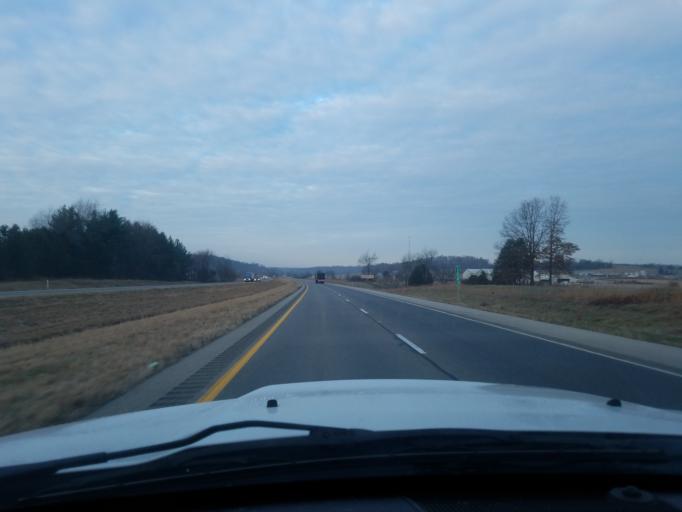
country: US
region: Indiana
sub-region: Harrison County
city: Corydon
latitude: 38.2422
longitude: -86.1740
